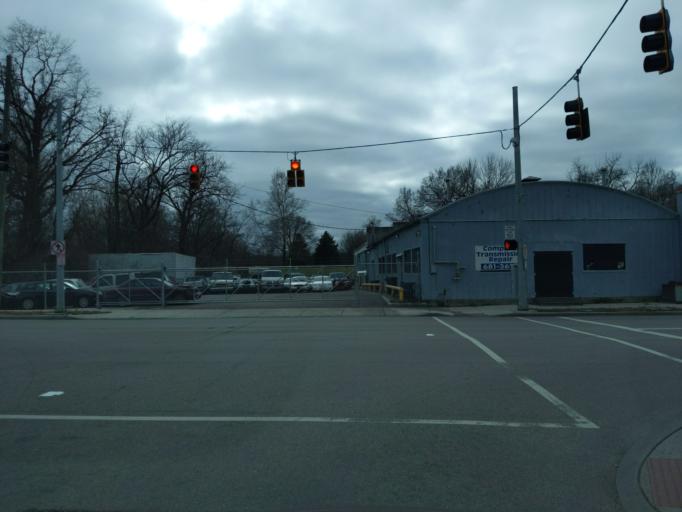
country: US
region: Ohio
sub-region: Hamilton County
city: Finneytown
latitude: 39.1625
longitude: -84.5483
